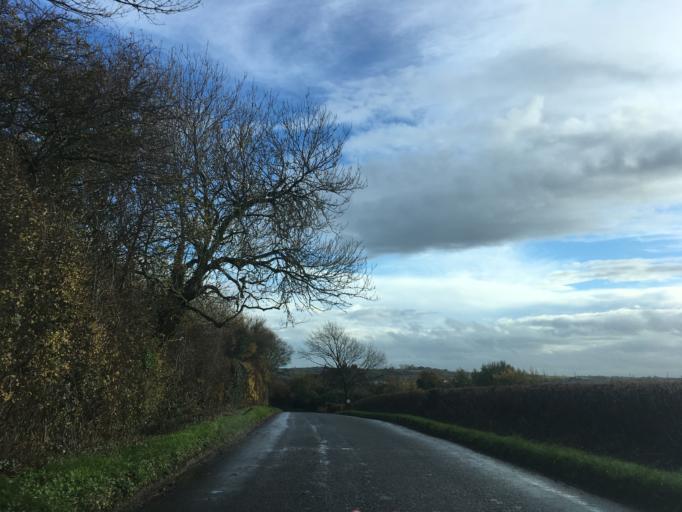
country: GB
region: England
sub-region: South Gloucestershire
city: Winterbourne
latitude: 51.5091
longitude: -2.4778
